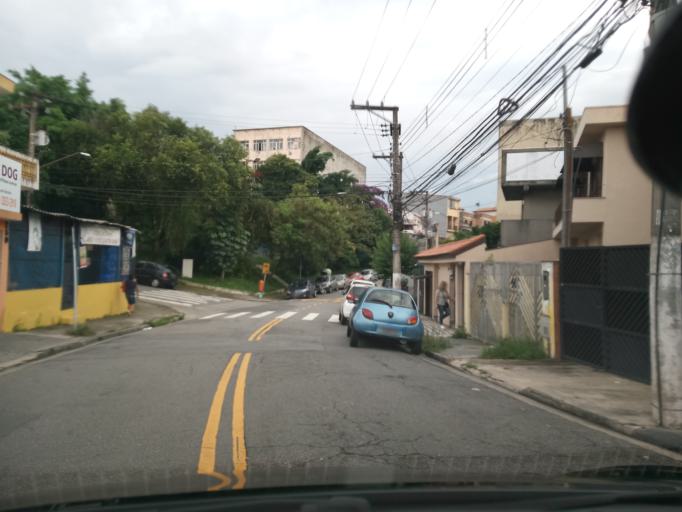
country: BR
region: Sao Paulo
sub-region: Sao Bernardo Do Campo
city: Sao Bernardo do Campo
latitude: -23.7119
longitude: -46.5576
